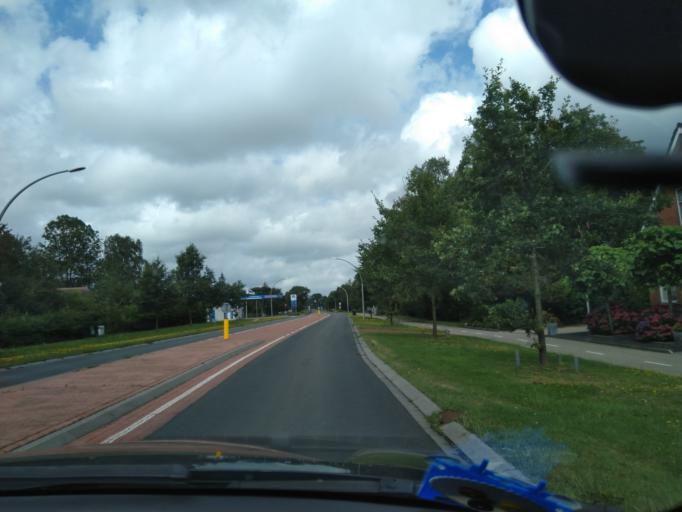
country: NL
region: Groningen
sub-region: Gemeente Groningen
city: Groningen
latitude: 53.1918
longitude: 6.5113
